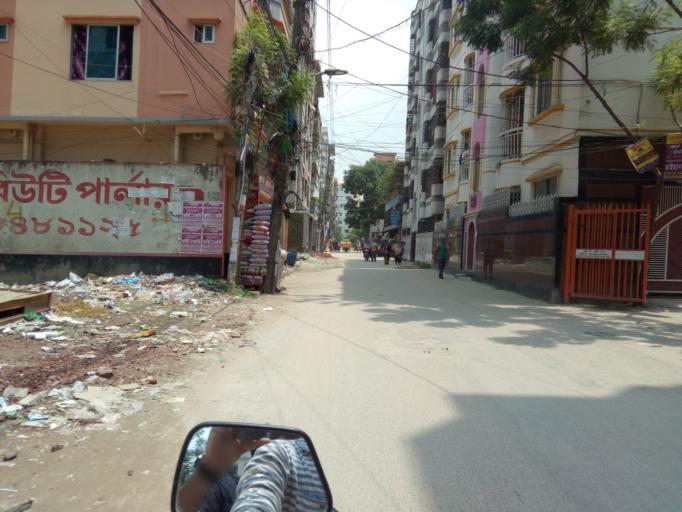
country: BD
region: Dhaka
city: Paltan
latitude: 23.7513
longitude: 90.4402
